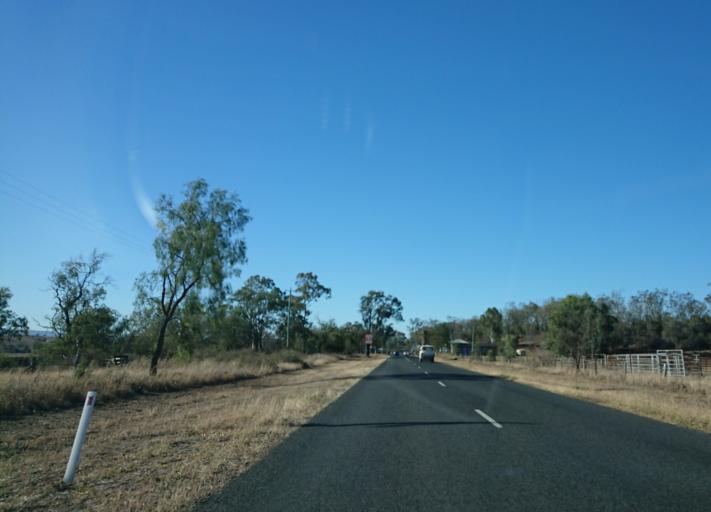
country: AU
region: Queensland
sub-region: Lockyer Valley
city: Gatton
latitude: -27.6338
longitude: 152.1868
